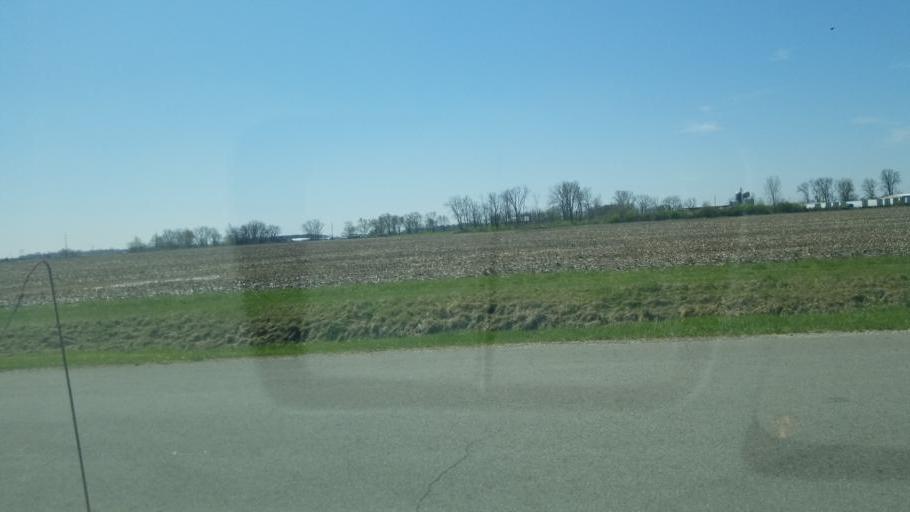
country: US
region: Ohio
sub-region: Marion County
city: Marion
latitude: 40.6355
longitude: -83.0790
